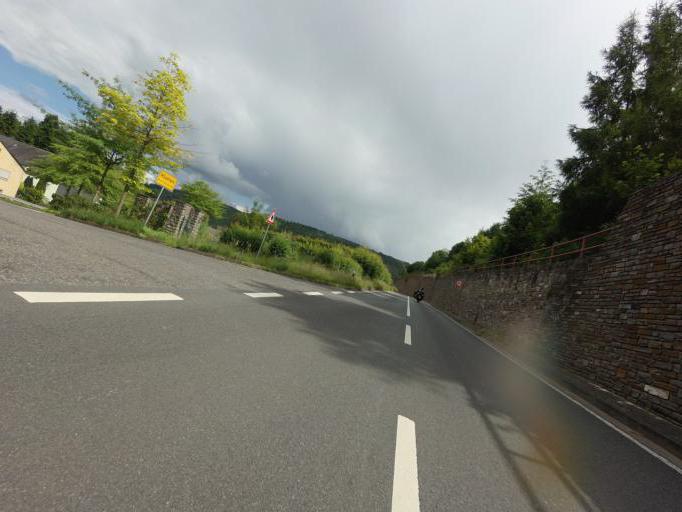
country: DE
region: Rheinland-Pfalz
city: Klotten
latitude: 50.1676
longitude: 7.1969
